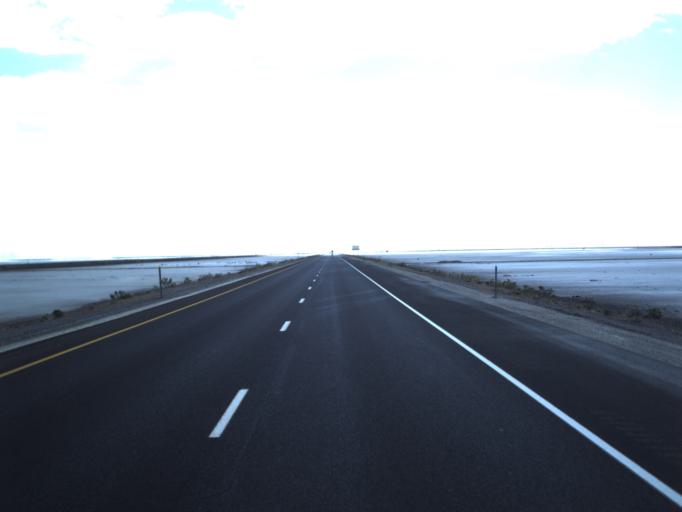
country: US
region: Utah
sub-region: Tooele County
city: Wendover
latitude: 40.7318
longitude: -113.5393
